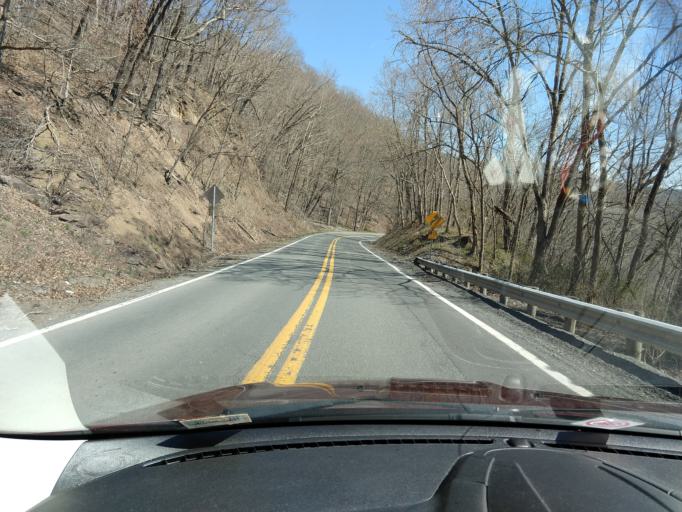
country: US
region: West Virginia
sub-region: Summers County
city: Hinton
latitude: 37.7351
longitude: -80.9033
